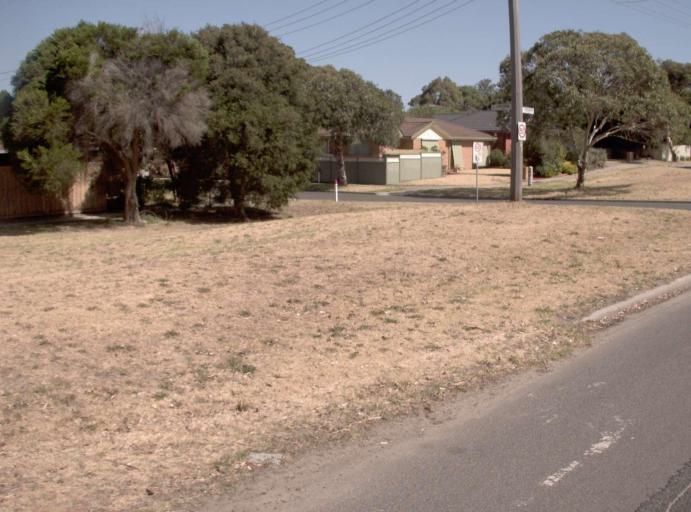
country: AU
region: Victoria
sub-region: Frankston
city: Carrum Downs
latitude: -38.0931
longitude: 145.1780
